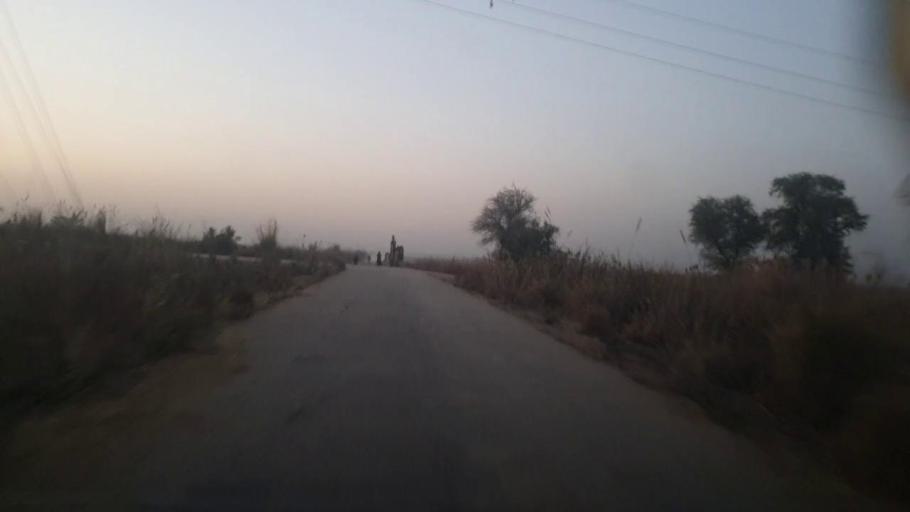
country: PK
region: Sindh
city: Kandiari
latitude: 26.6881
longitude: 68.9273
